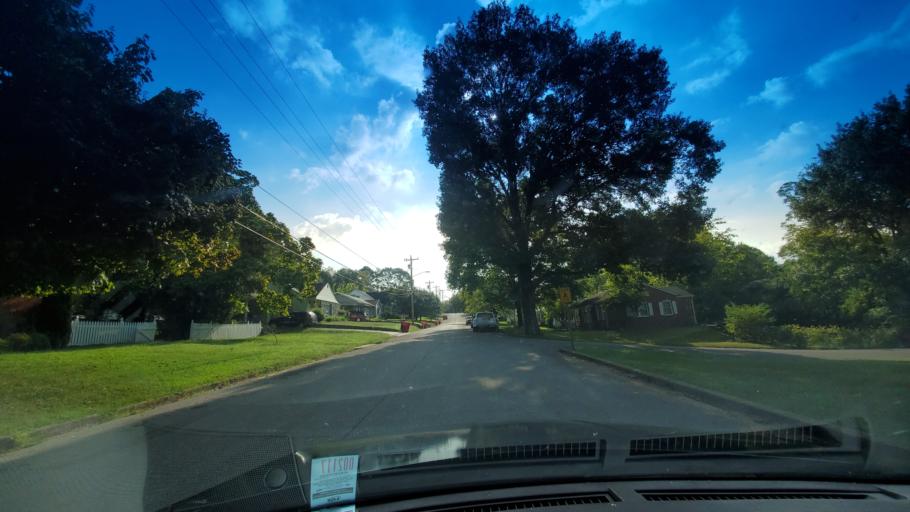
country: US
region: Tennessee
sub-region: Smith County
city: Carthage
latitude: 36.2573
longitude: -85.9430
